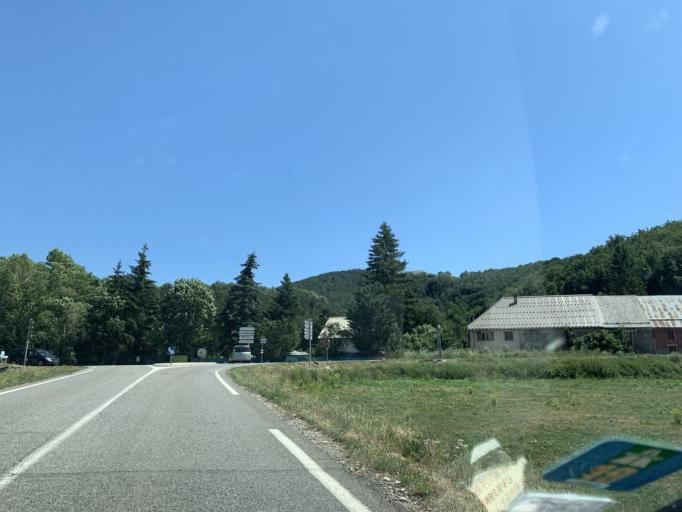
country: FR
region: Provence-Alpes-Cote d'Azur
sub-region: Departement des Hautes-Alpes
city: Saint-Bonnet-en-Champsaur
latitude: 44.6387
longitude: 6.1422
